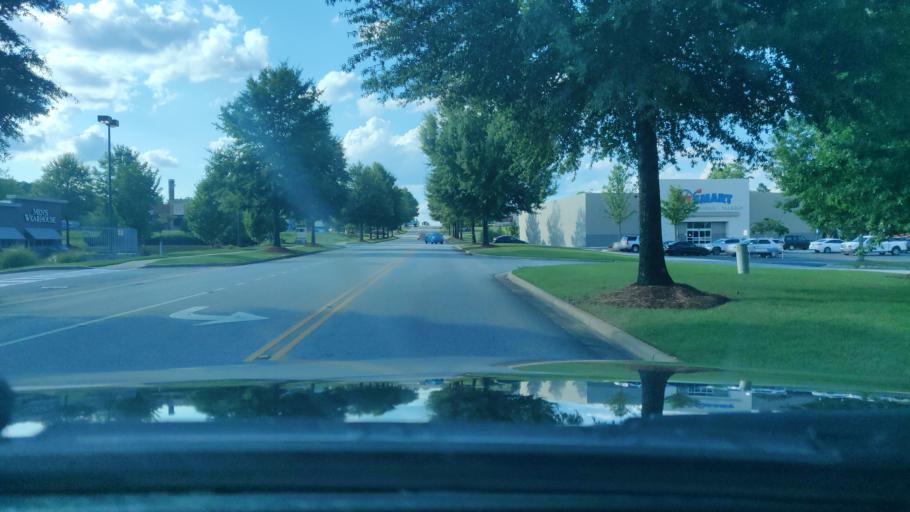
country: US
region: Alabama
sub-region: Lee County
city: Opelika
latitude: 32.6193
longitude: -85.4086
